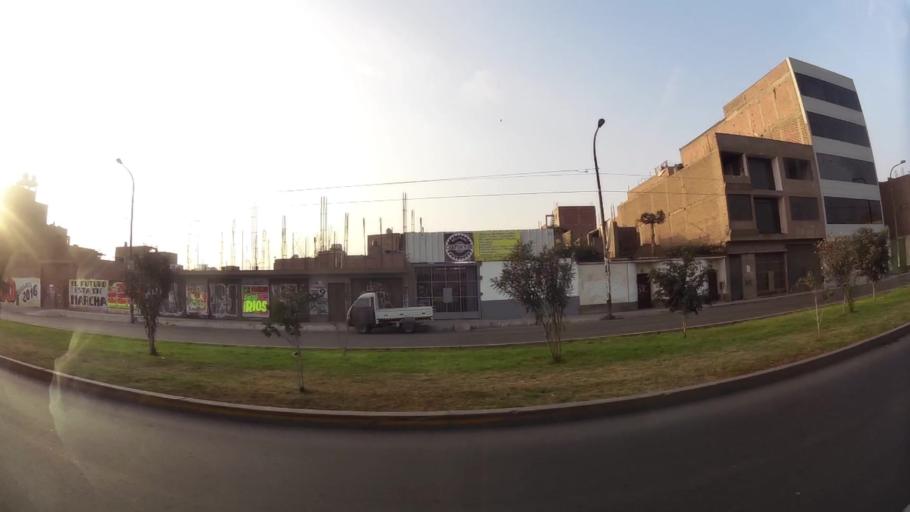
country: PE
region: Lima
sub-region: Lima
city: Independencia
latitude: -11.9894
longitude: -77.0912
